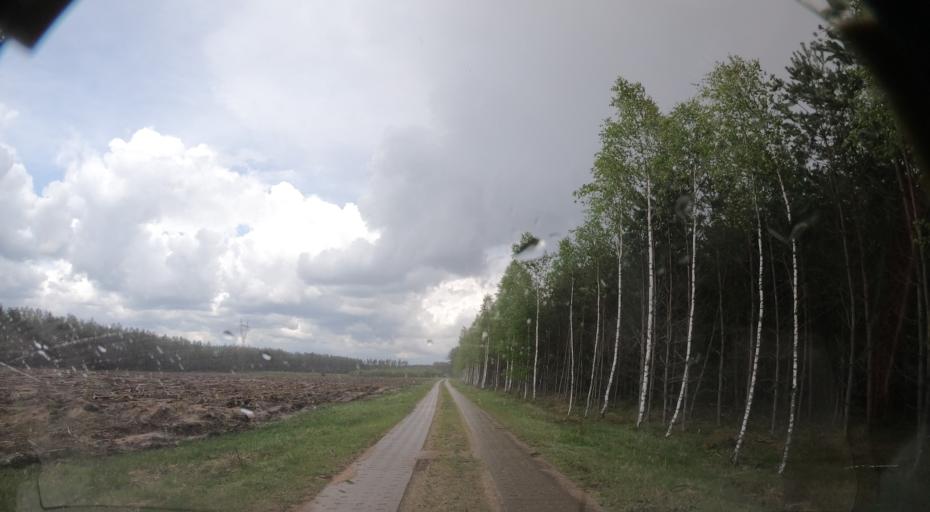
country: PL
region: West Pomeranian Voivodeship
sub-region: Powiat koszalinski
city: Bobolice
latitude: 54.0631
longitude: 16.4243
